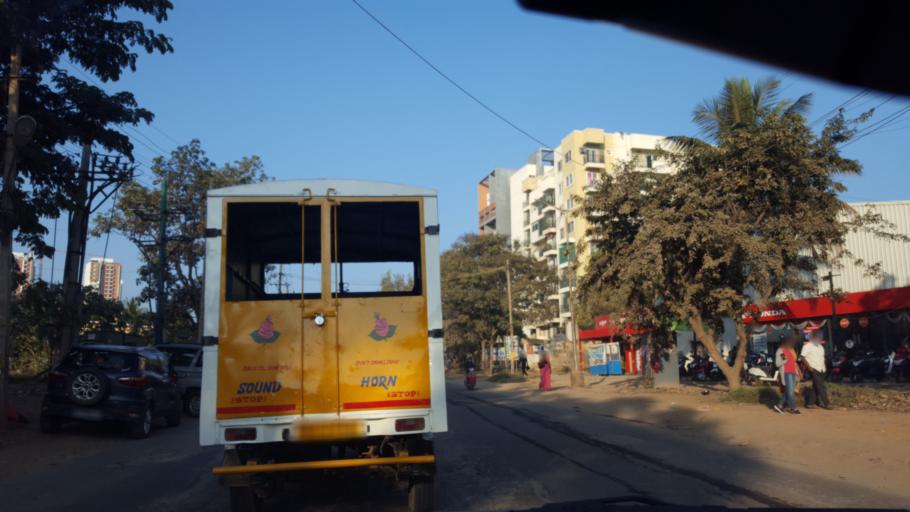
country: IN
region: Karnataka
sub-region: Bangalore Urban
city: Bangalore
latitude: 12.9288
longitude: 77.7396
